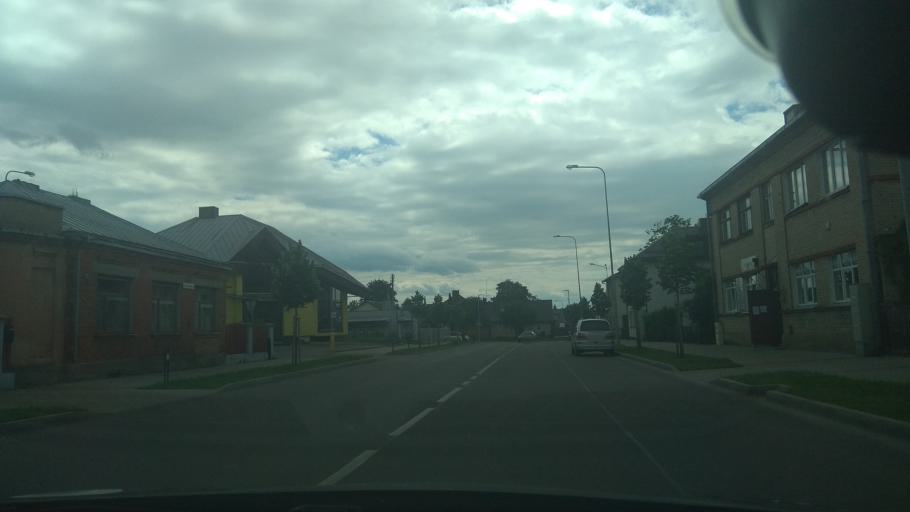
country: LT
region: Marijampoles apskritis
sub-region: Marijampole Municipality
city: Marijampole
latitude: 54.5524
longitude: 23.3536
